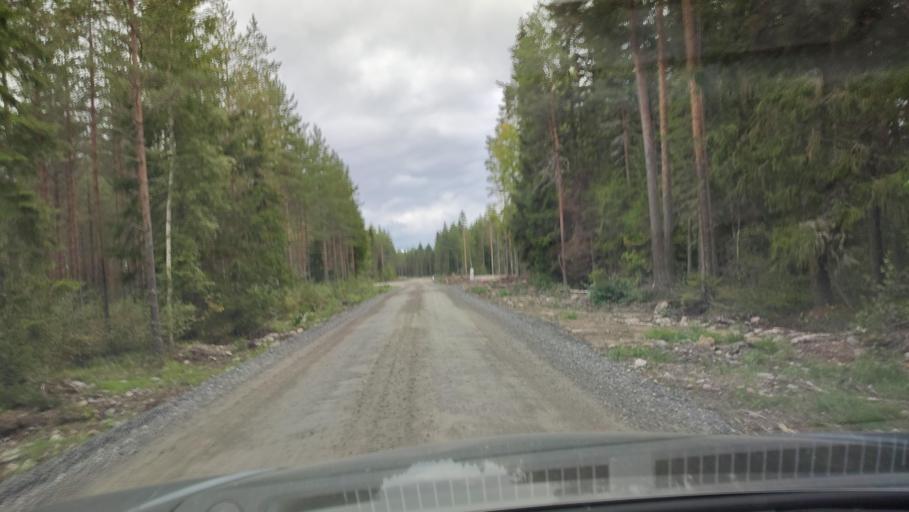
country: FI
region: Southern Ostrobothnia
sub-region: Suupohja
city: Karijoki
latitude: 62.1874
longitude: 21.5890
